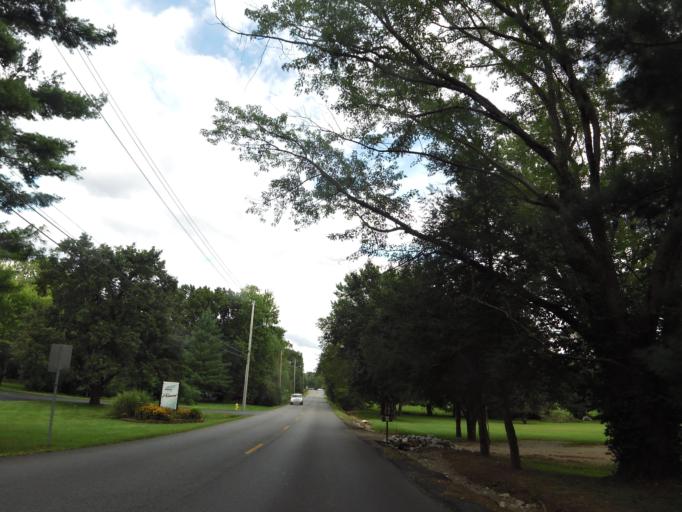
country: US
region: Kentucky
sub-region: Christian County
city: Hopkinsville
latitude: 36.8509
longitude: -87.5149
